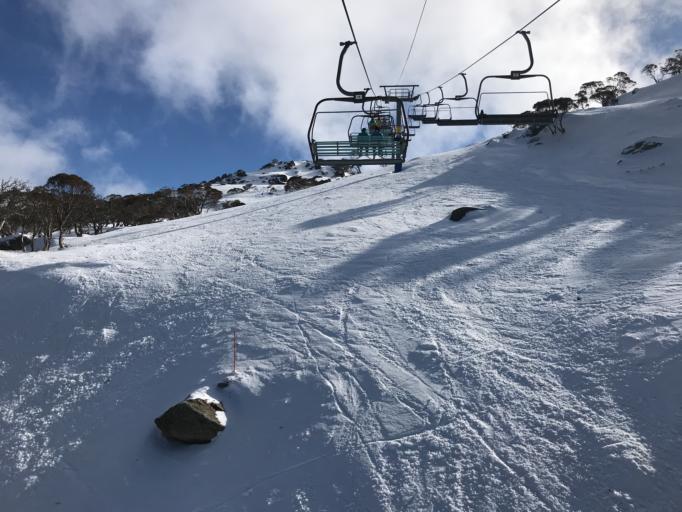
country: AU
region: New South Wales
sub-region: Snowy River
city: Jindabyne
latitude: -36.3934
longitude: 148.4033
